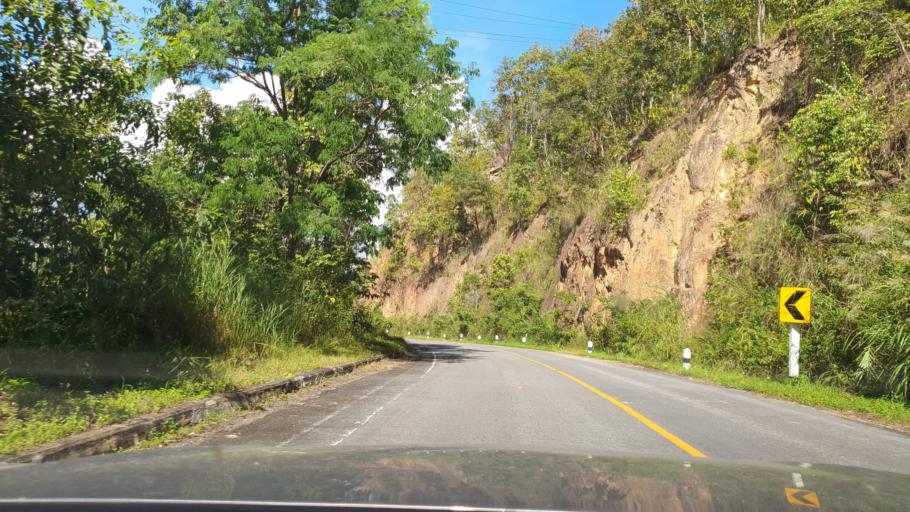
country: TH
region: Chiang Mai
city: Phrao
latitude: 19.3594
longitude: 99.2700
